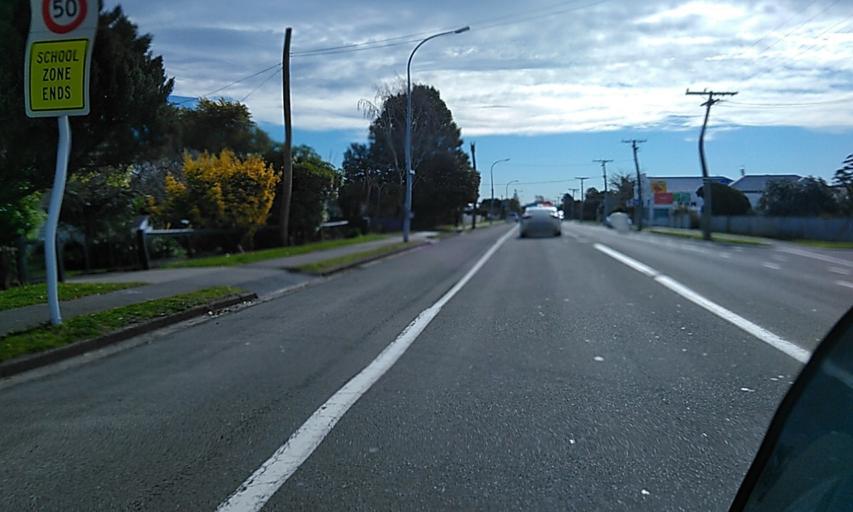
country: NZ
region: Gisborne
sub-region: Gisborne District
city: Gisborne
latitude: -38.6475
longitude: 178.0175
